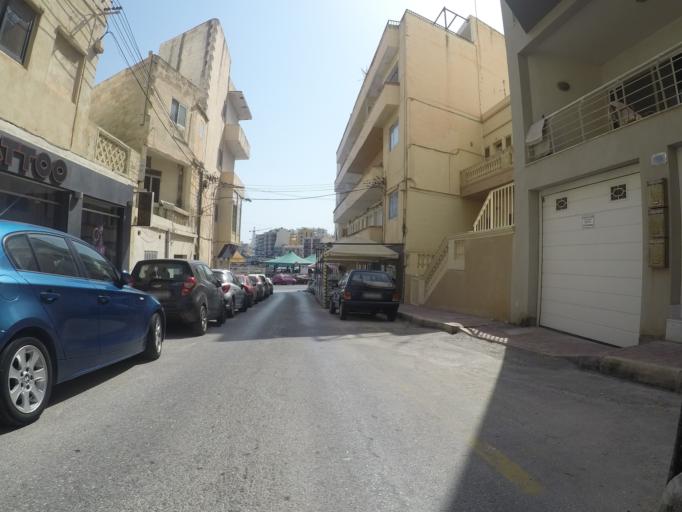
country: MT
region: Saint Paul's Bay
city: San Pawl il-Bahar
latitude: 35.9520
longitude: 14.4122
